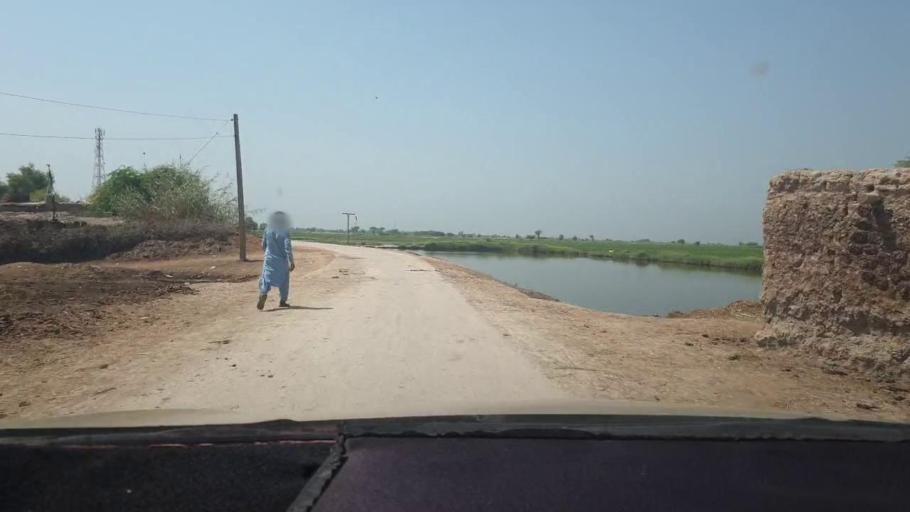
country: PK
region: Sindh
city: Miro Khan
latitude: 27.6614
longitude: 68.0820
